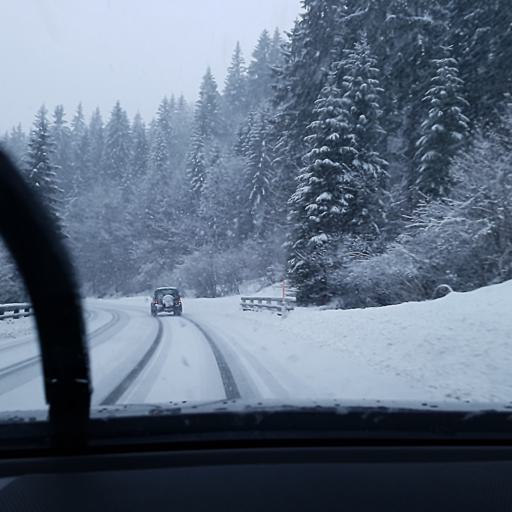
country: AT
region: Salzburg
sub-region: Politischer Bezirk Hallein
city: Abtenau
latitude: 47.5795
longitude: 13.4076
